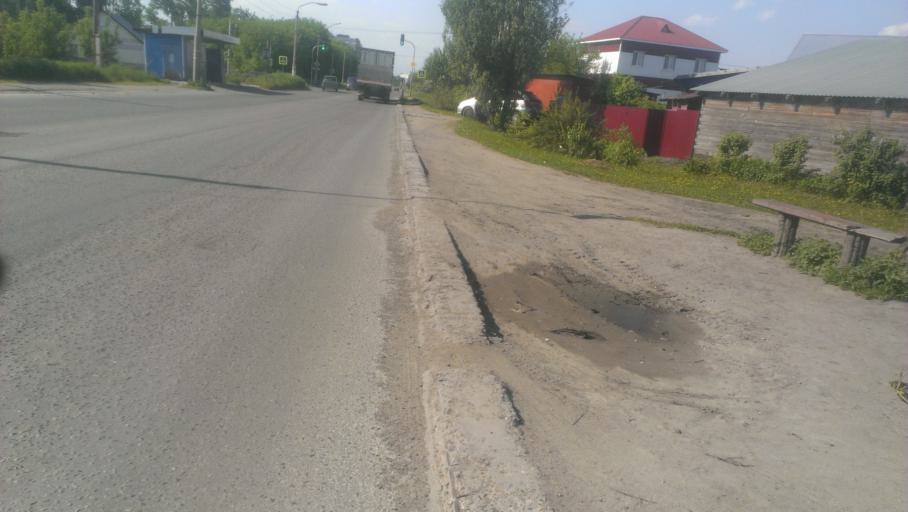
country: RU
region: Altai Krai
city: Novoaltaysk
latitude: 53.4066
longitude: 83.9444
